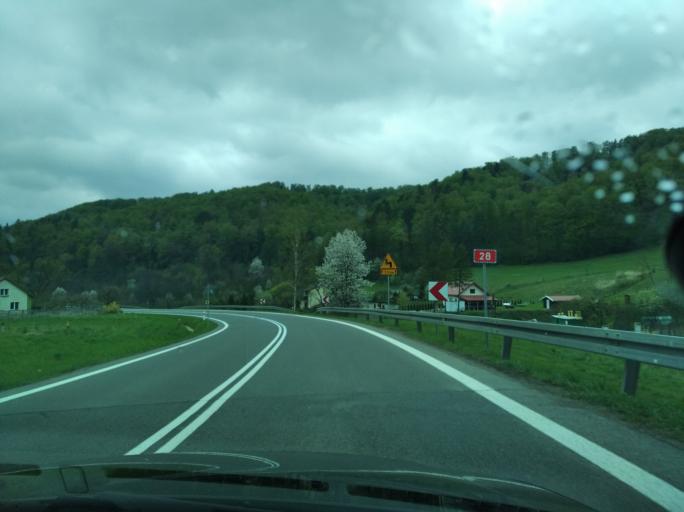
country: PL
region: Subcarpathian Voivodeship
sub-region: Powiat sanocki
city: Zagorz
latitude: 49.5447
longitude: 22.3032
